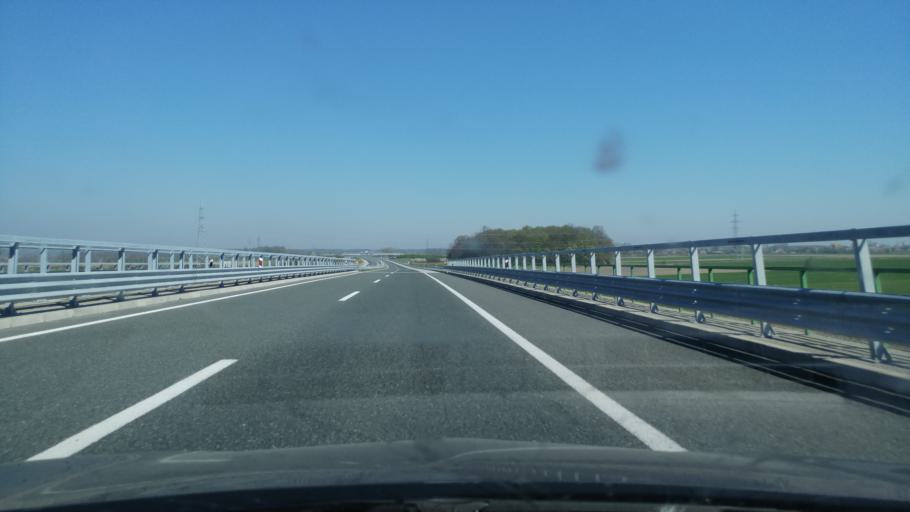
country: HR
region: Brodsko-Posavska
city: Vrpolje
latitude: 45.2053
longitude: 18.3333
